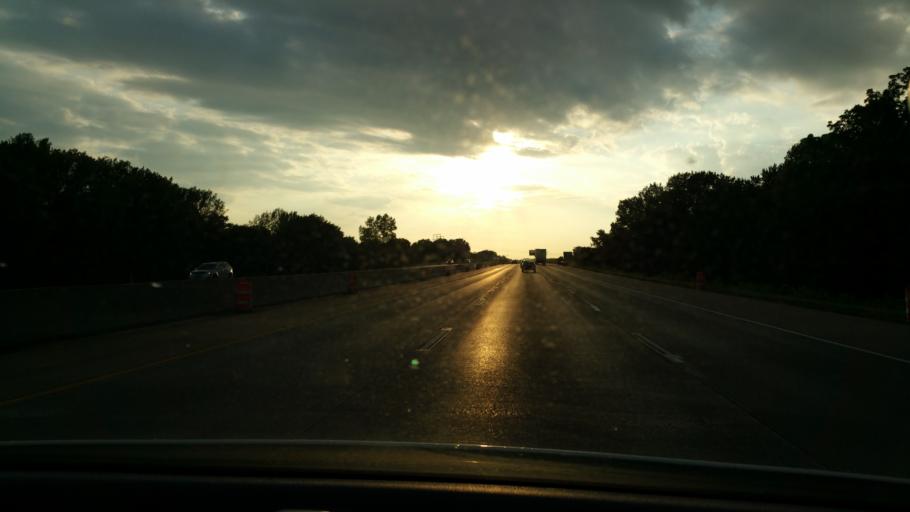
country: US
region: Iowa
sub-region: Polk County
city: Johnston
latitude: 41.6507
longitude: -93.6625
